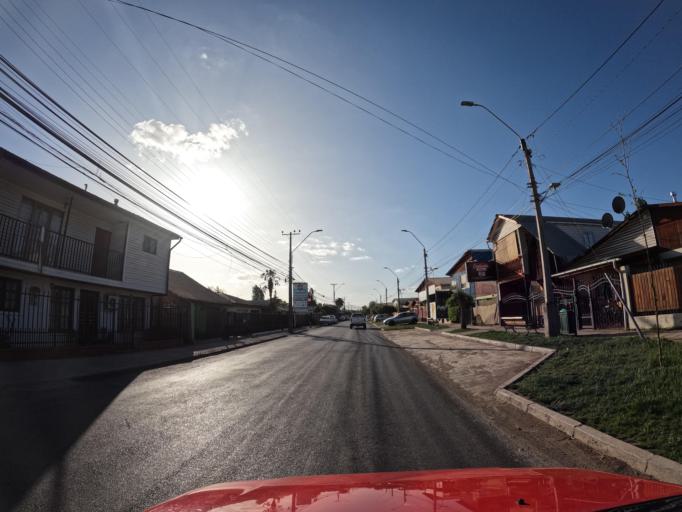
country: CL
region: O'Higgins
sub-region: Provincia de Colchagua
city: Santa Cruz
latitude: -34.6472
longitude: -71.3617
